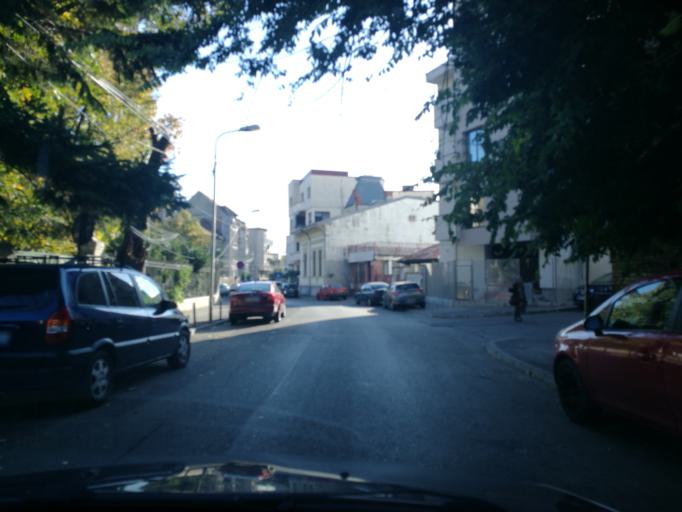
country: RO
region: Bucuresti
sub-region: Municipiul Bucuresti
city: Bucharest
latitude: 44.4457
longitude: 26.1094
